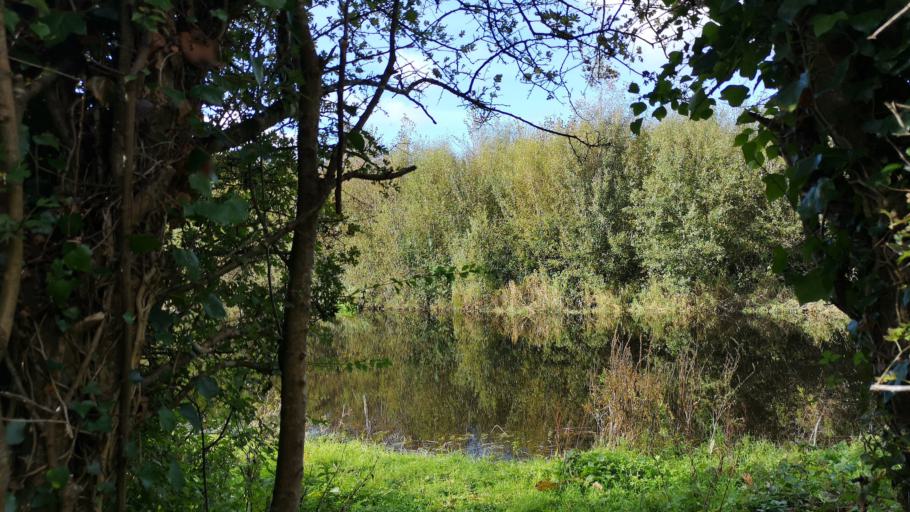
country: IE
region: Connaught
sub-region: County Galway
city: Gort
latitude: 53.0726
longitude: -8.8107
